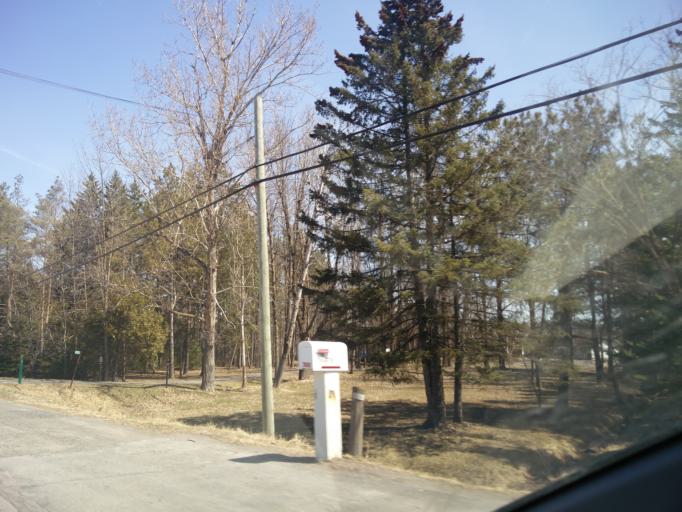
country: CA
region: Ontario
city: Bells Corners
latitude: 45.1838
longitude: -75.6380
